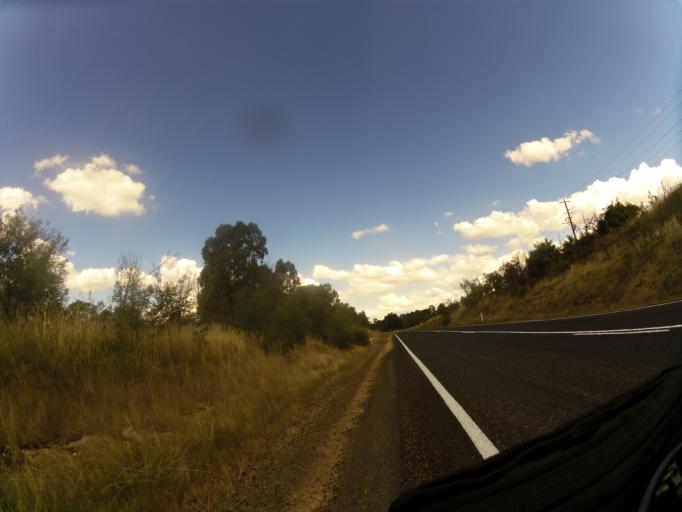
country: AU
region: Victoria
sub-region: Mansfield
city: Mansfield
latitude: -36.9076
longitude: 145.9981
